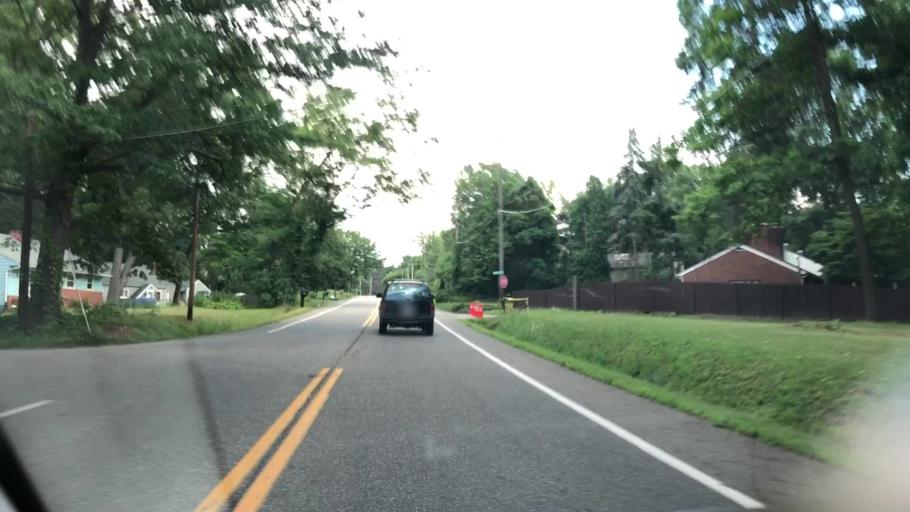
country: US
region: Ohio
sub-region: Summit County
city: Portage Lakes
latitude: 40.9933
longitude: -81.5526
